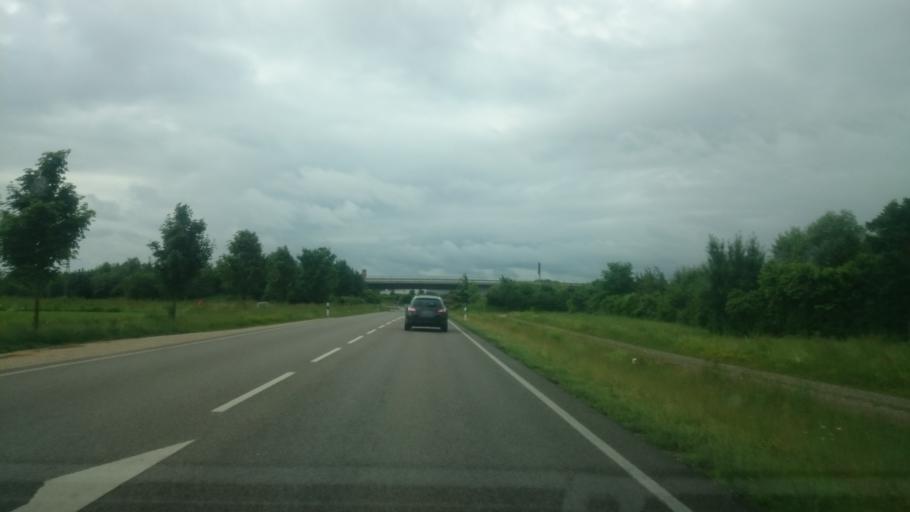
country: DE
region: Bavaria
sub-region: Swabia
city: Friedberg
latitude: 48.3653
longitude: 10.9586
